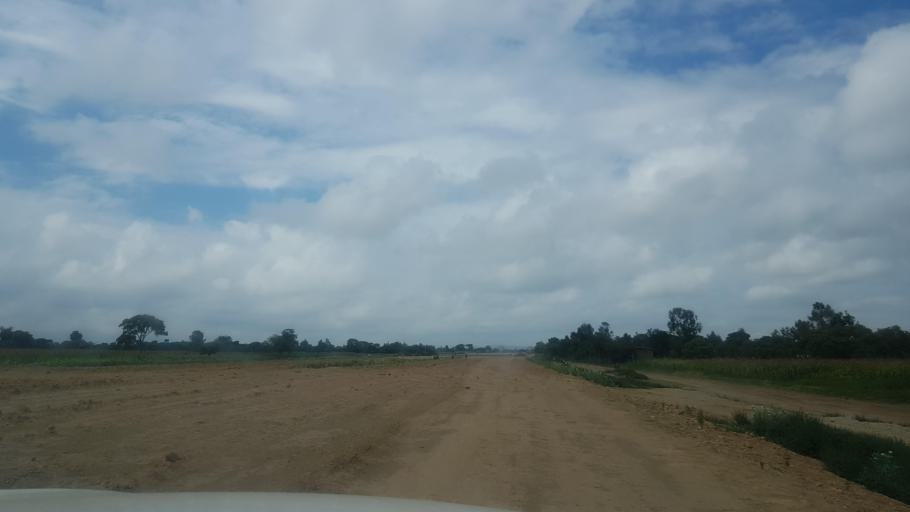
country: ET
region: Oromiya
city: Shashemene
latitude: 7.2657
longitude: 38.5971
